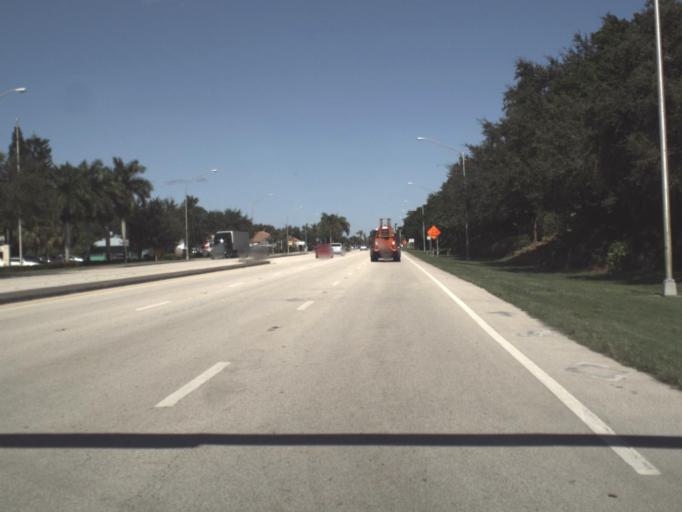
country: US
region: Florida
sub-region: Collier County
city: Naples Park
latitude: 26.2617
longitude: -81.8013
